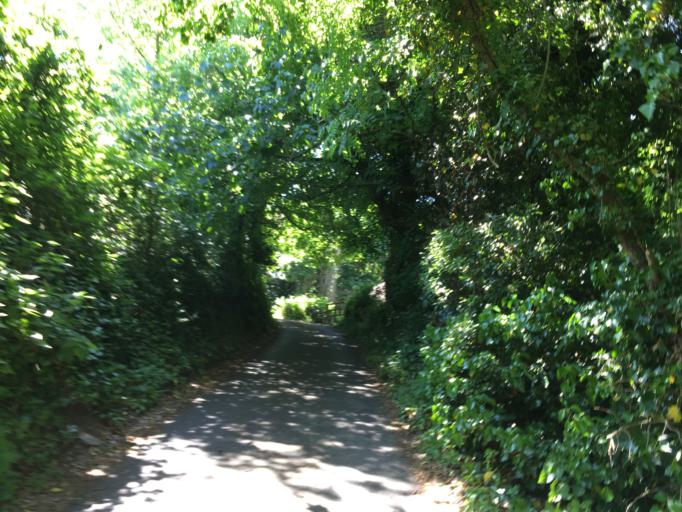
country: GB
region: England
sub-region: Devon
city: Dartmouth
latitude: 50.3456
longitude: -3.5629
